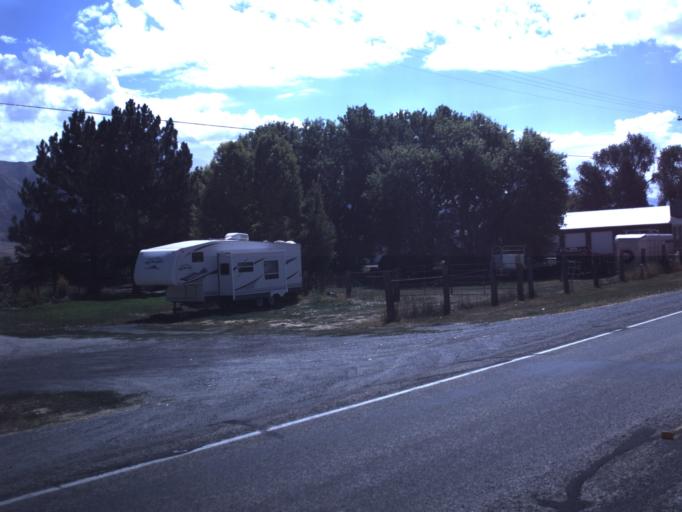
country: US
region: Utah
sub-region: Box Elder County
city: Garland
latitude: 41.7519
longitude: -112.1484
